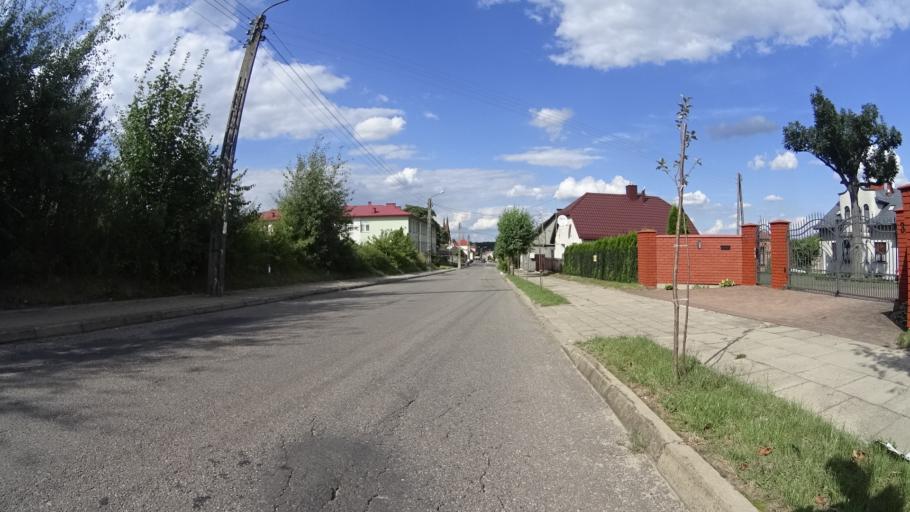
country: PL
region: Masovian Voivodeship
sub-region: Powiat grojecki
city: Mogielnica
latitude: 51.6898
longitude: 20.7209
